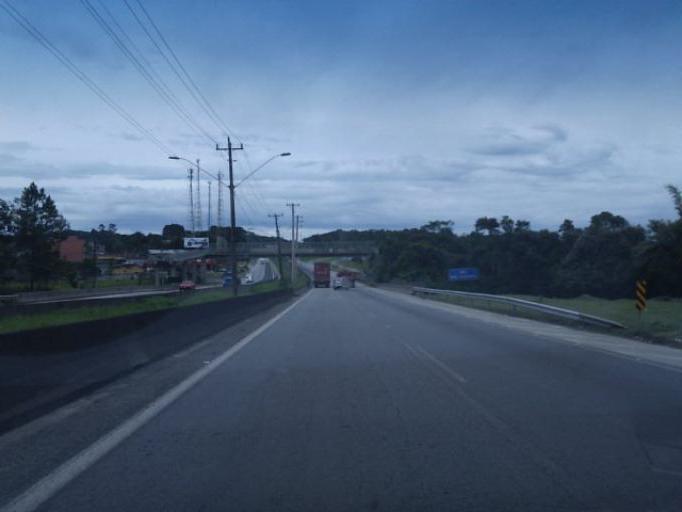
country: BR
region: Sao Paulo
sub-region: Juquitiba
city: Juquitiba
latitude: -23.9204
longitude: -46.9912
